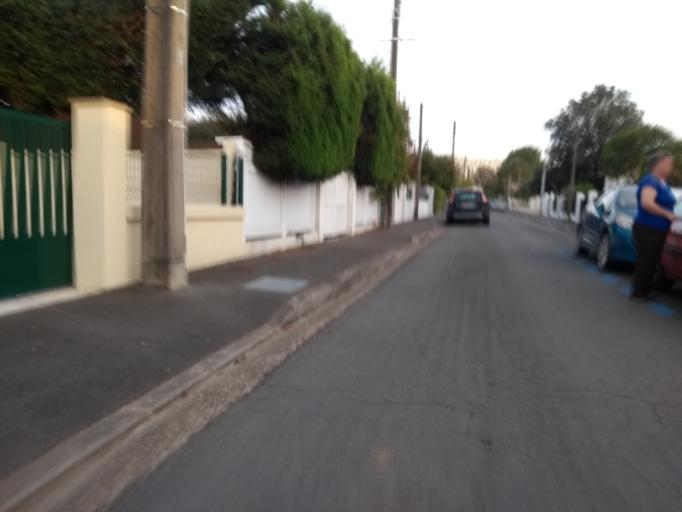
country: FR
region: Aquitaine
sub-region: Departement de la Gironde
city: Talence
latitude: 44.7984
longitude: -0.6051
